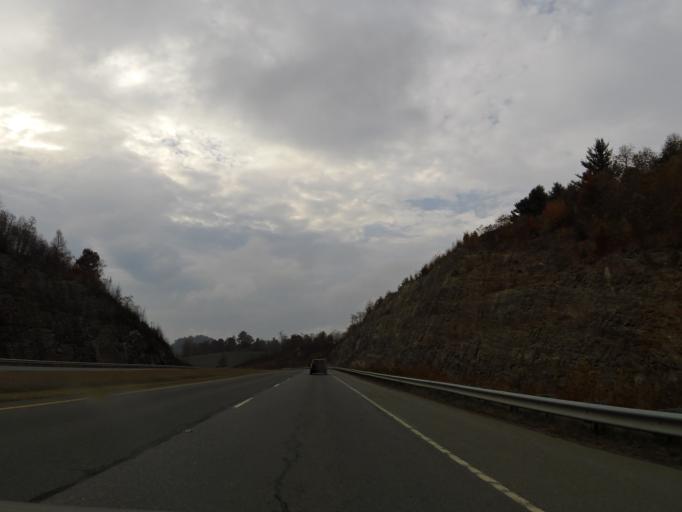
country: US
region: North Carolina
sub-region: Watauga County
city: Boone
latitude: 36.2306
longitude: -81.5885
